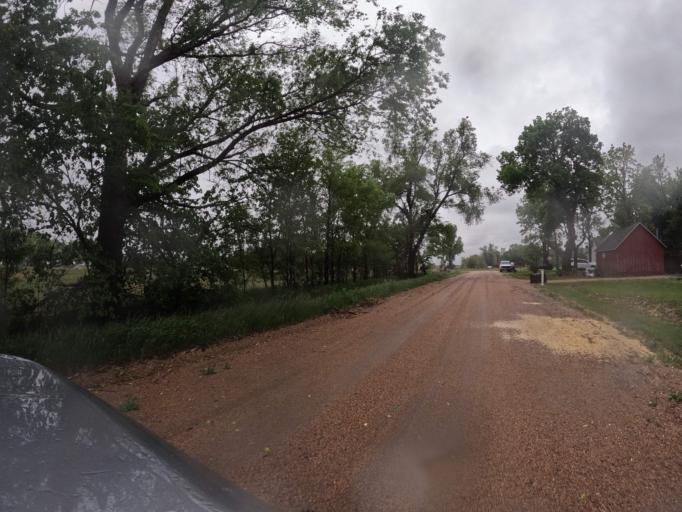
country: US
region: Nebraska
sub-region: Clay County
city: Harvard
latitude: 40.6187
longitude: -98.1040
